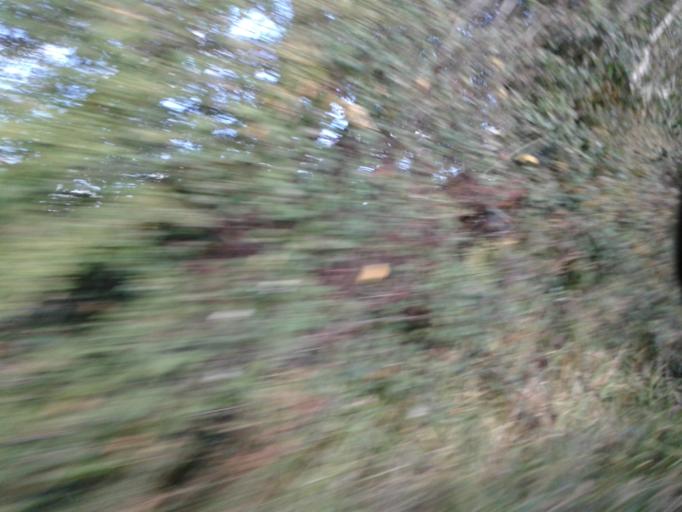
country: IE
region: Leinster
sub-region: An Mhi
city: Slane
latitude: 53.6885
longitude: -6.4974
